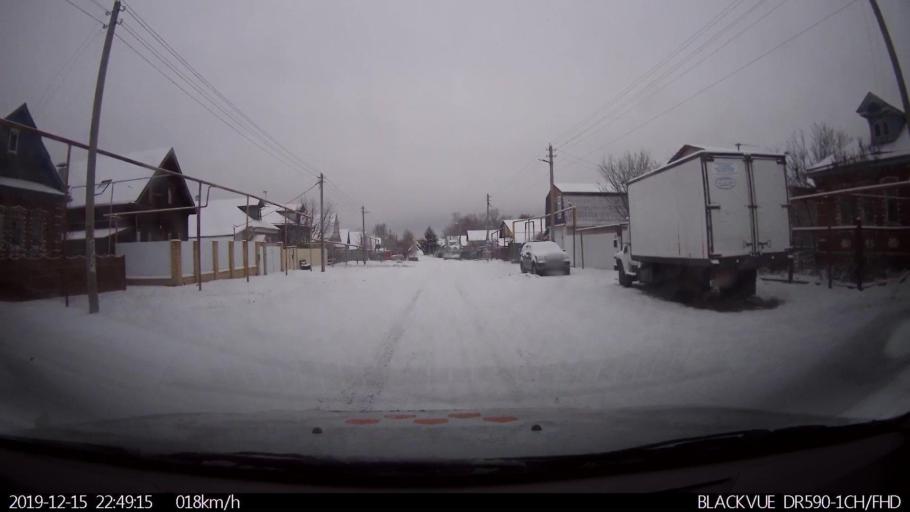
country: RU
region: Nizjnij Novgorod
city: Afonino
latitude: 56.2206
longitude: 44.1128
